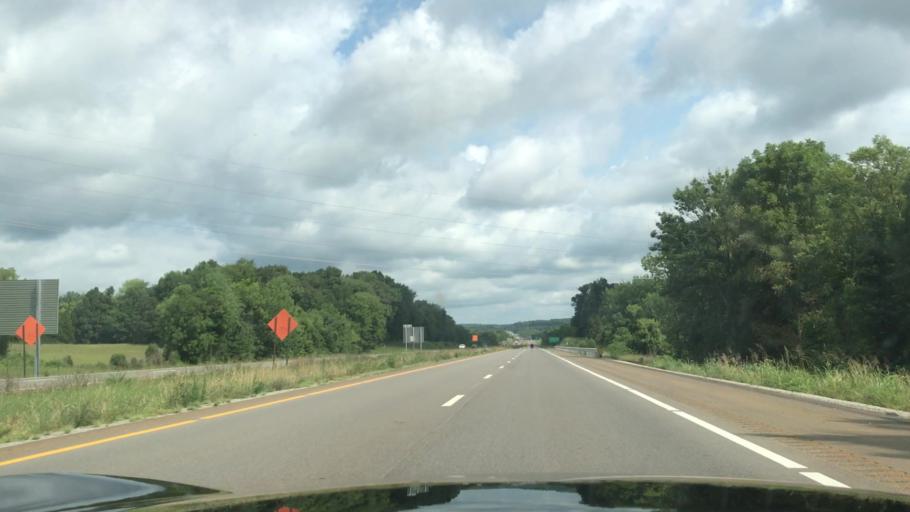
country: US
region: Kentucky
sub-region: Warren County
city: Bowling Green
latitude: 36.9696
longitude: -86.4993
